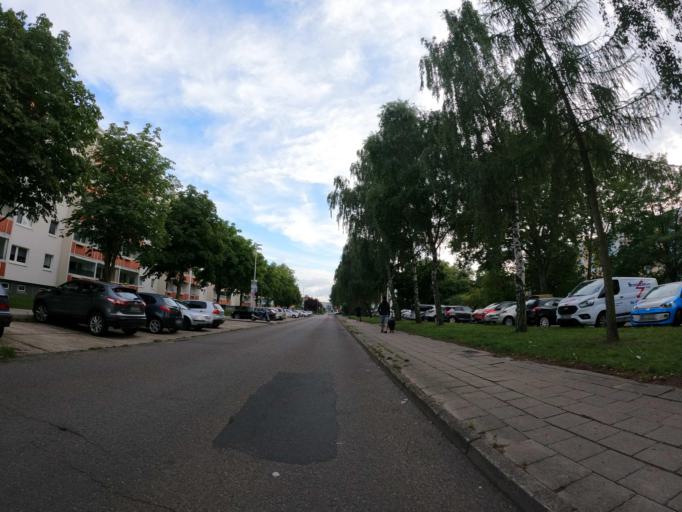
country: DE
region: Mecklenburg-Vorpommern
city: Kramerhof
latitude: 54.3275
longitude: 13.0541
